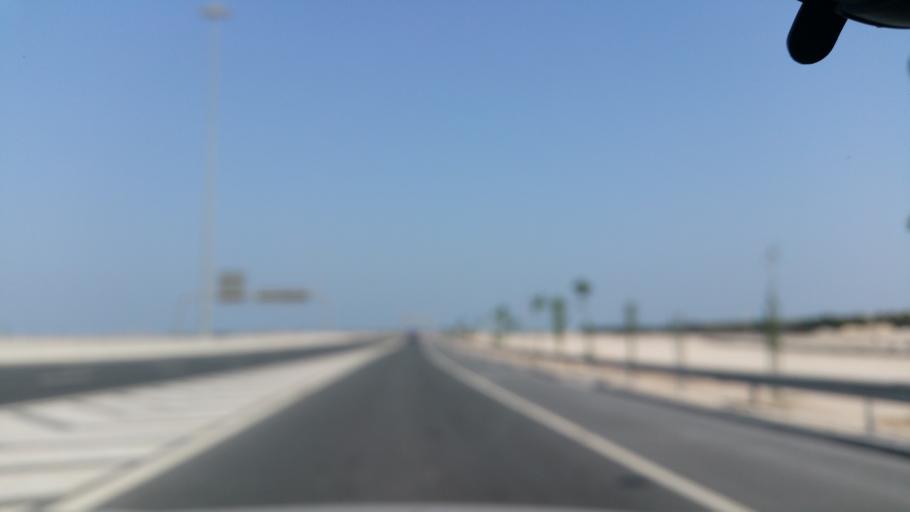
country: QA
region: Baladiyat Umm Salal
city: Umm Salal `Ali
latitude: 25.4567
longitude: 51.4838
